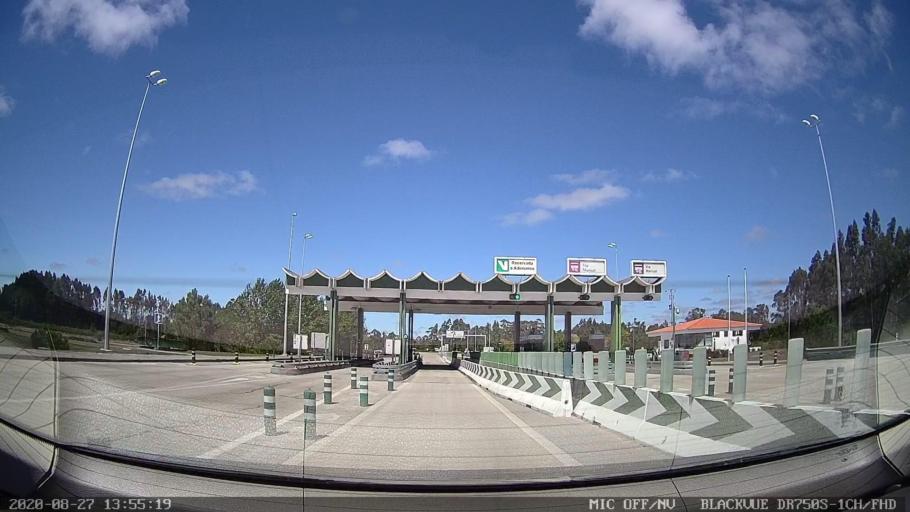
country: PT
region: Coimbra
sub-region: Montemor-O-Velho
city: Arazede
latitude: 40.3290
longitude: -8.7251
